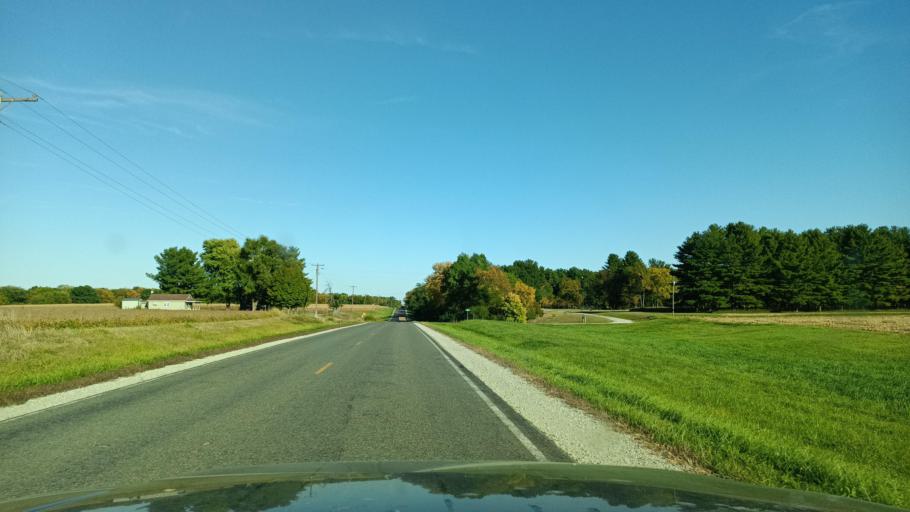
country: US
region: Illinois
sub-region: De Witt County
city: Clinton
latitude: 40.2245
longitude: -88.8364
